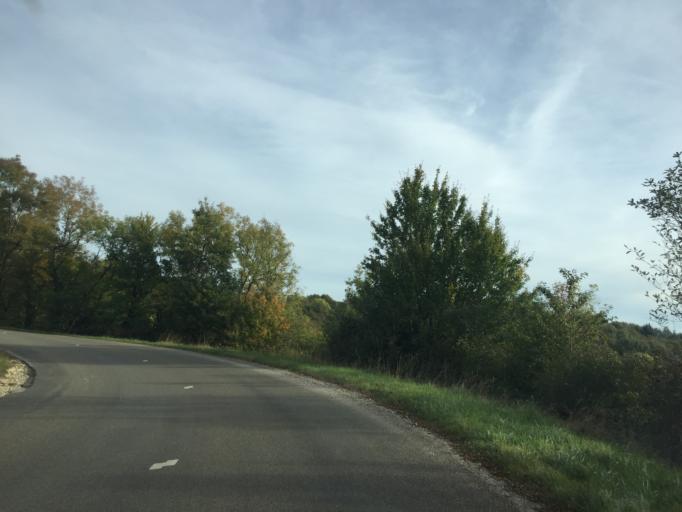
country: FR
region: Franche-Comte
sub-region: Departement du Jura
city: Orgelet
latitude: 46.4996
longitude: 5.5075
